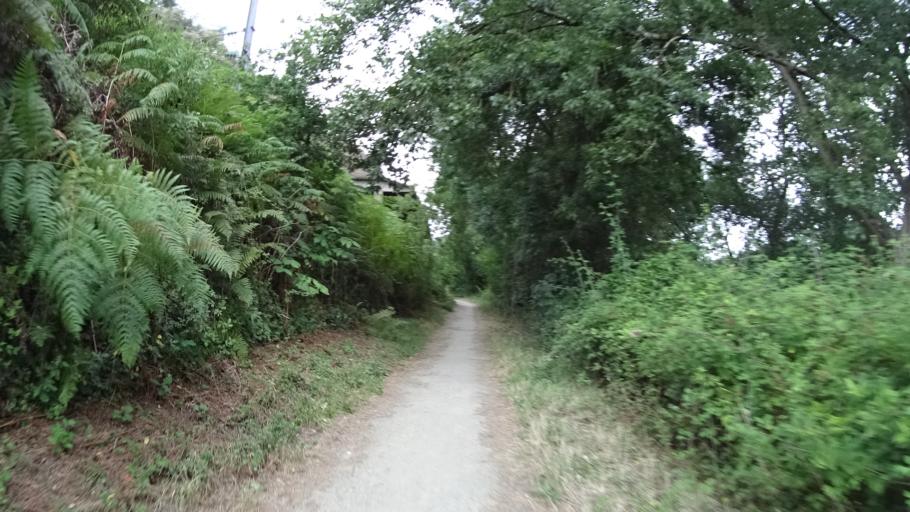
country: FR
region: Pays de la Loire
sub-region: Departement de Maine-et-Loire
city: La Varenne
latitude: 47.3359
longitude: -1.3113
